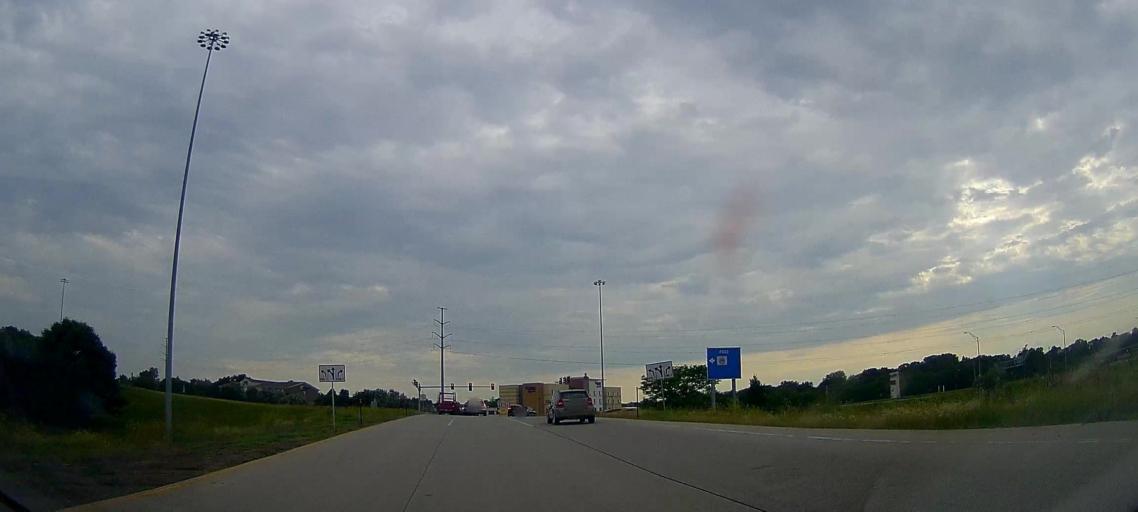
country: US
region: Nebraska
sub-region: Douglas County
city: Bennington
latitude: 41.3239
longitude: -96.0692
